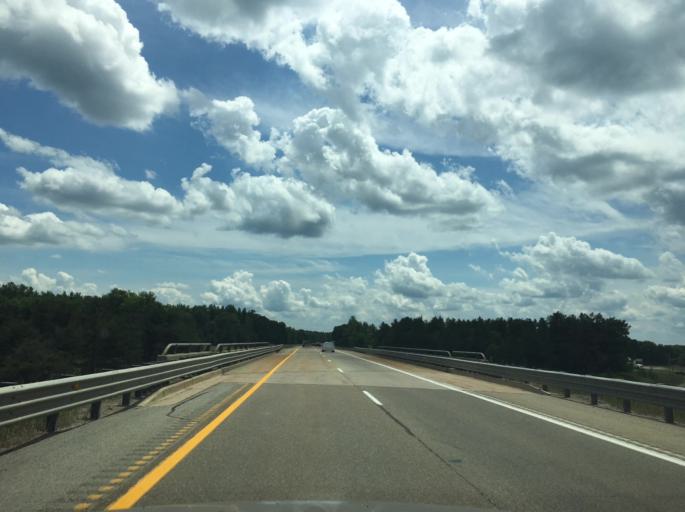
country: US
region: Michigan
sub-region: Crawford County
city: Grayling
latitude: 44.5721
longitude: -84.7095
